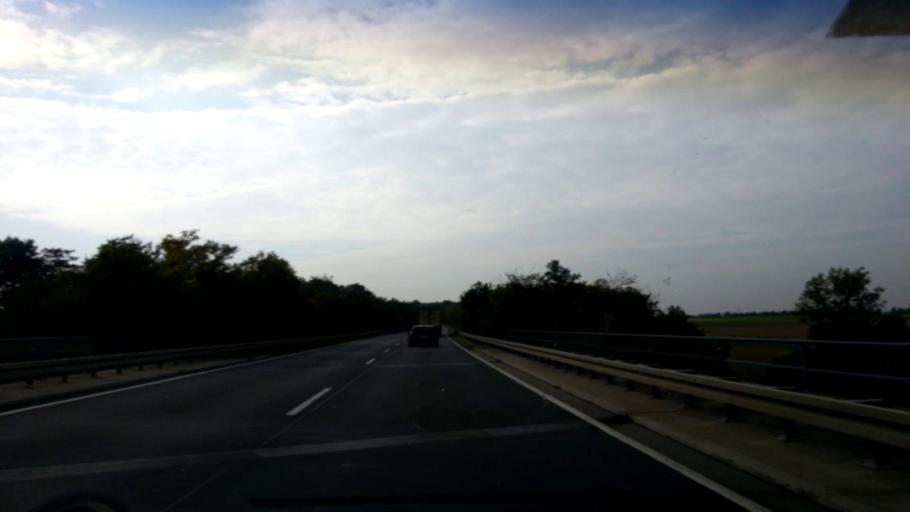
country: DE
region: Bavaria
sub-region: Regierungsbezirk Unterfranken
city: Prichsenstadt
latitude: 49.8368
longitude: 10.3535
